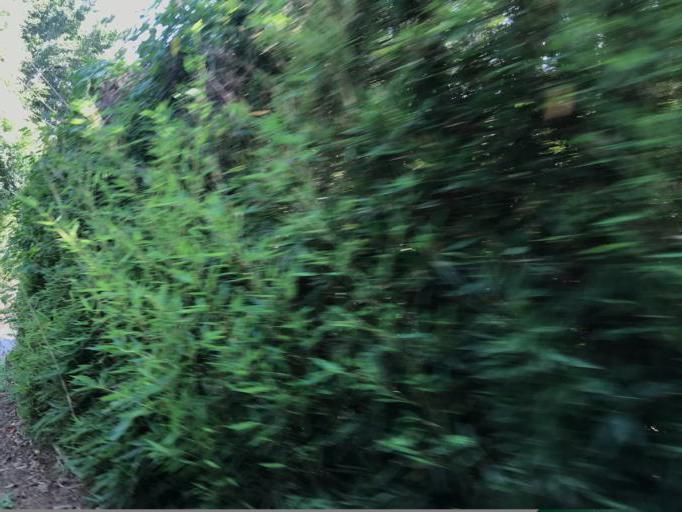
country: CO
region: Valle del Cauca
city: Cali
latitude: 3.4709
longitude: -76.6208
